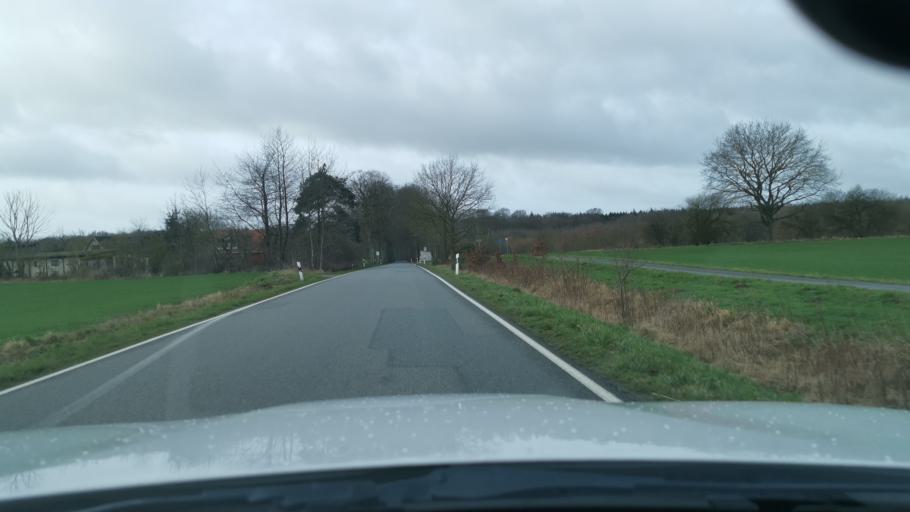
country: DE
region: Mecklenburg-Vorpommern
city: Wardow
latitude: 54.0037
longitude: 12.3924
